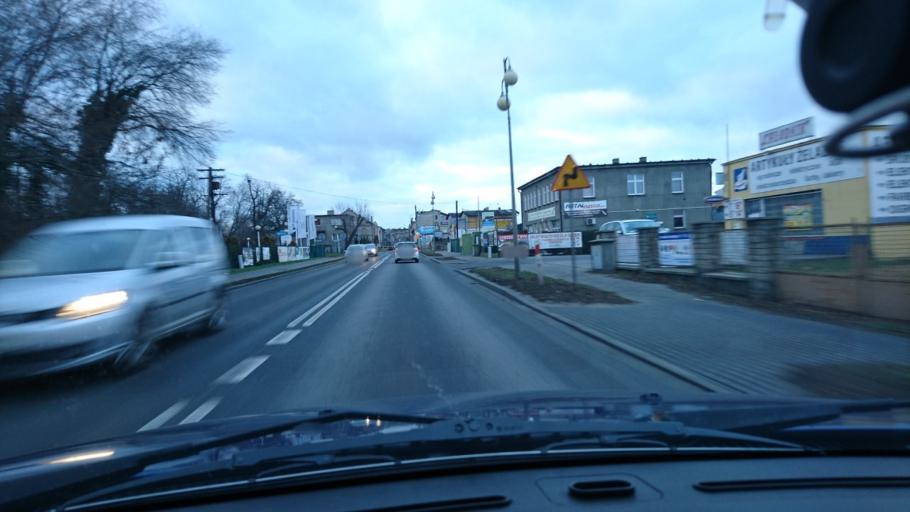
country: PL
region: Greater Poland Voivodeship
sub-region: Powiat kepinski
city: Kepno
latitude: 51.2747
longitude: 17.9902
